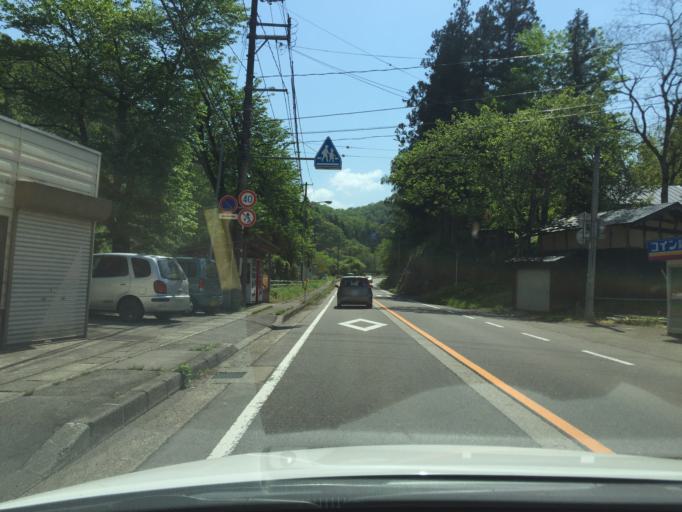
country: JP
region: Niigata
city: Kamo
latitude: 37.6266
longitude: 139.1008
